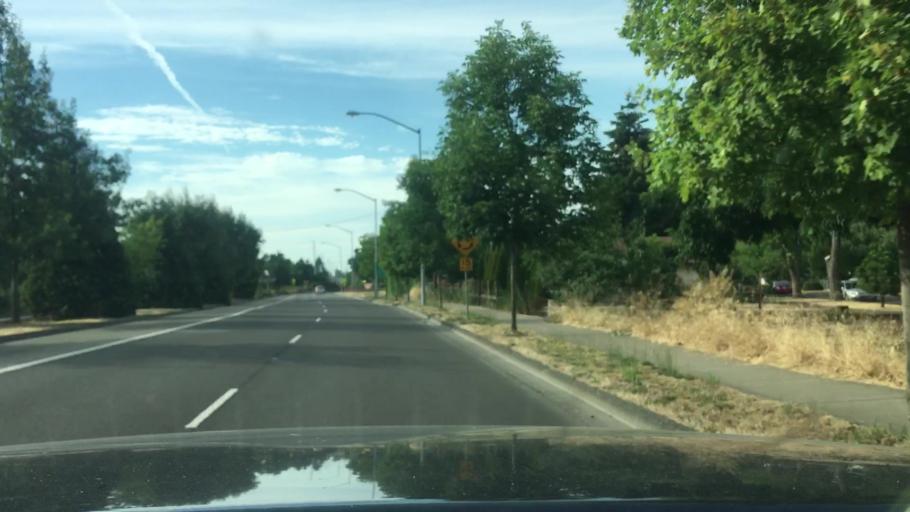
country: US
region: Oregon
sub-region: Lane County
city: Springfield
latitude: 44.0686
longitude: -123.0279
